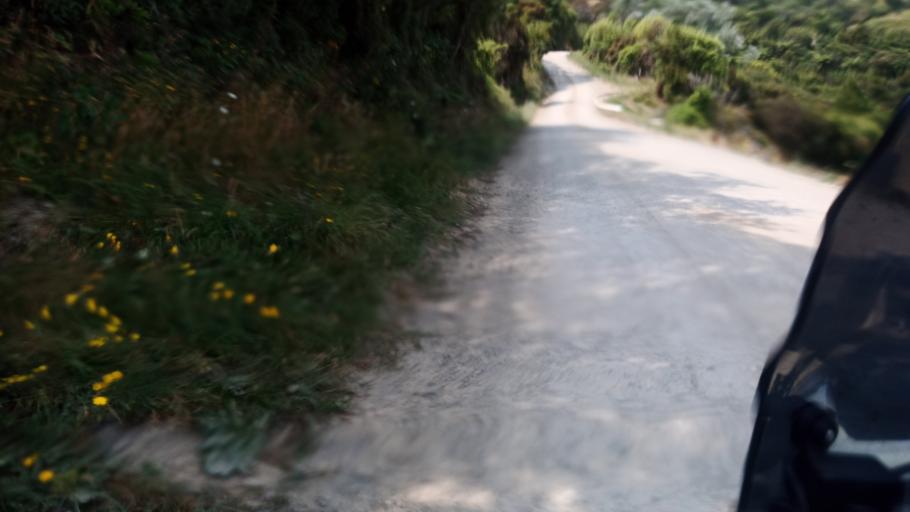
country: NZ
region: Bay of Plenty
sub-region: Opotiki District
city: Opotiki
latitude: -37.6455
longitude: 178.1373
